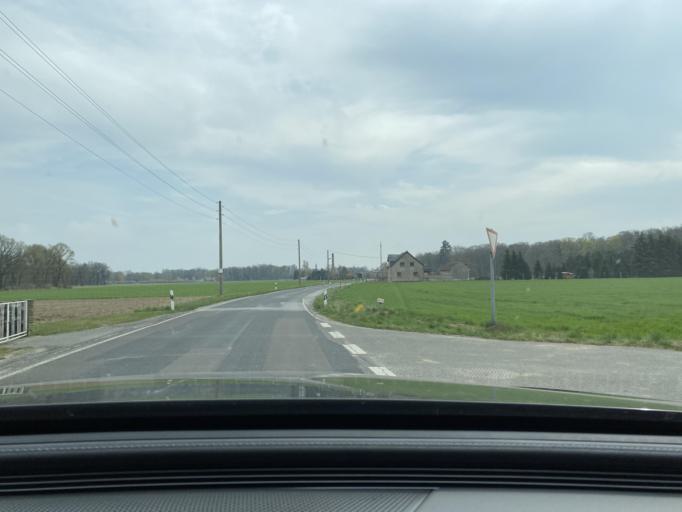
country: DE
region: Saxony
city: Neschwitz
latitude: 51.2839
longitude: 14.3203
